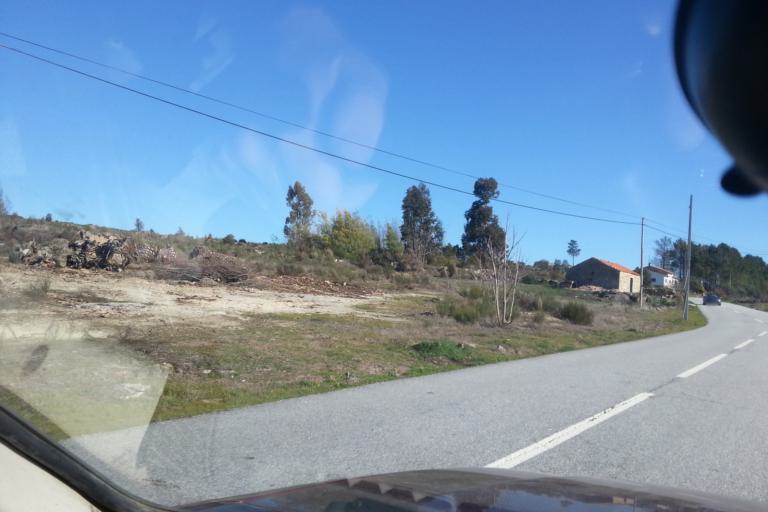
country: PT
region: Guarda
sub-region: Fornos de Algodres
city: Fornos de Algodres
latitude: 40.6045
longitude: -7.5215
